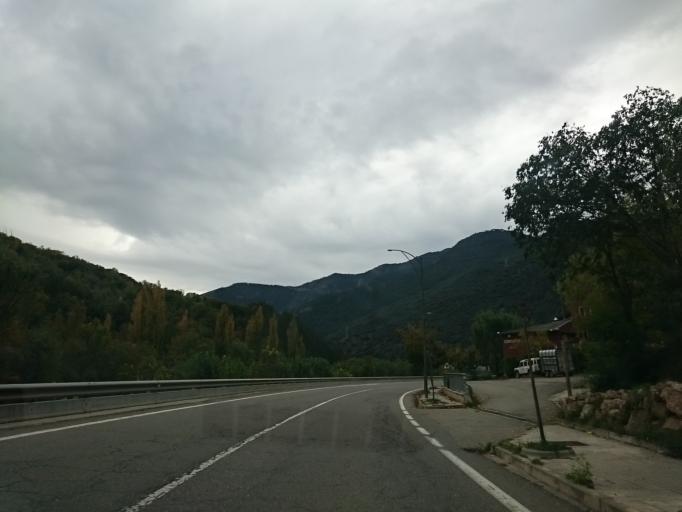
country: ES
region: Catalonia
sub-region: Provincia de Lleida
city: Sort
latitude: 42.3596
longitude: 1.0832
